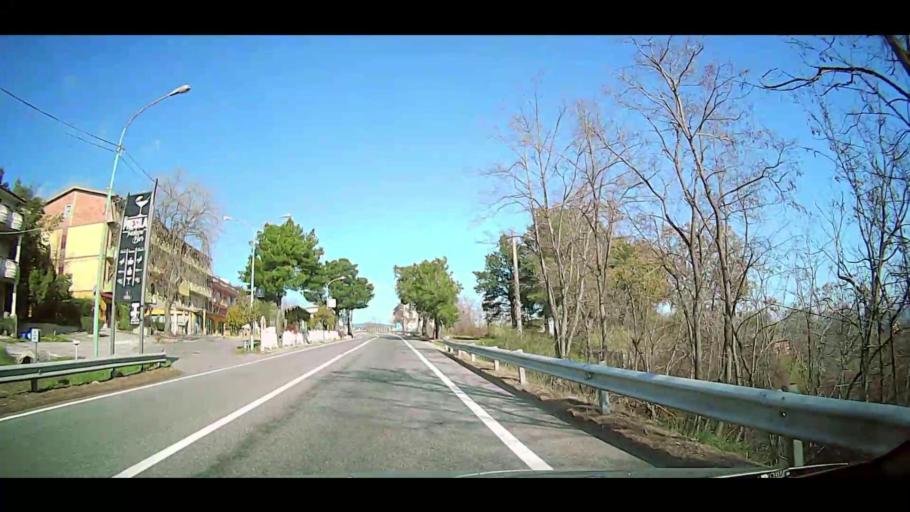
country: IT
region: Calabria
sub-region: Provincia di Crotone
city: Cerenzia
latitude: 39.2458
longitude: 16.7904
